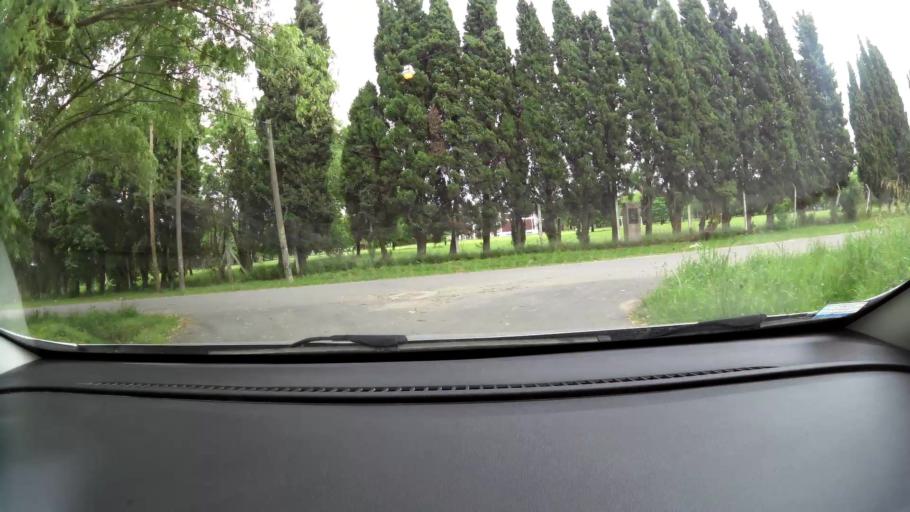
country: AR
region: Buenos Aires
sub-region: Partido de Campana
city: Campana
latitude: -34.1962
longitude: -58.9476
